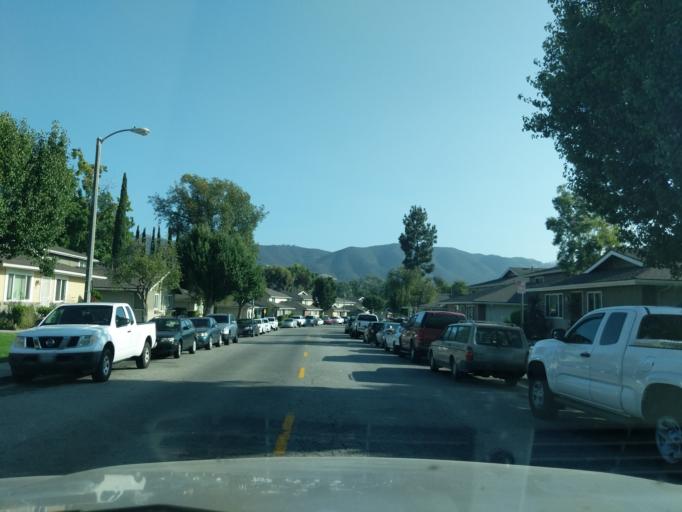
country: US
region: California
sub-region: Ventura County
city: Casa Conejo
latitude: 34.1873
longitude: -118.9134
